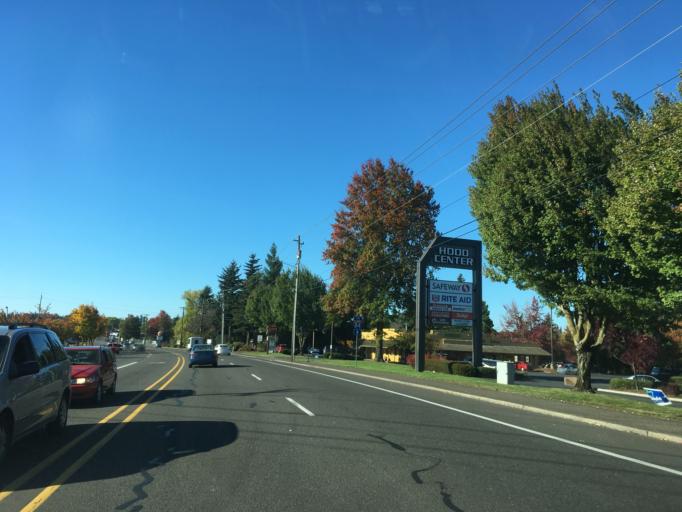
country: US
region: Oregon
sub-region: Multnomah County
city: Gresham
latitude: 45.5048
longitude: -122.4173
